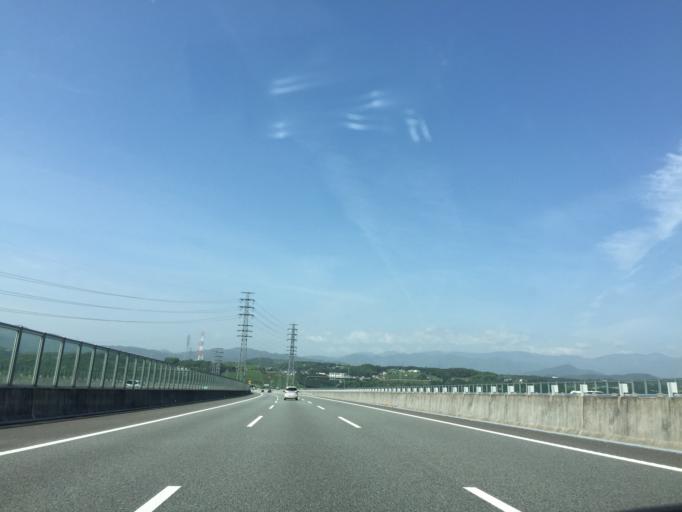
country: JP
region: Shizuoka
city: Fujinomiya
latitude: 35.2006
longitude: 138.6507
